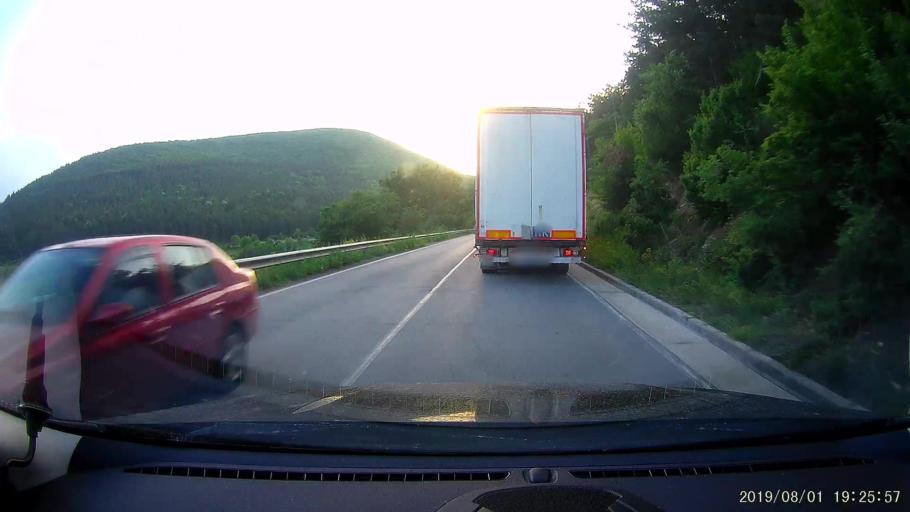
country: BG
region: Burgas
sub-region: Obshtina Sungurlare
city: Sungurlare
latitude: 42.8589
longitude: 26.9432
